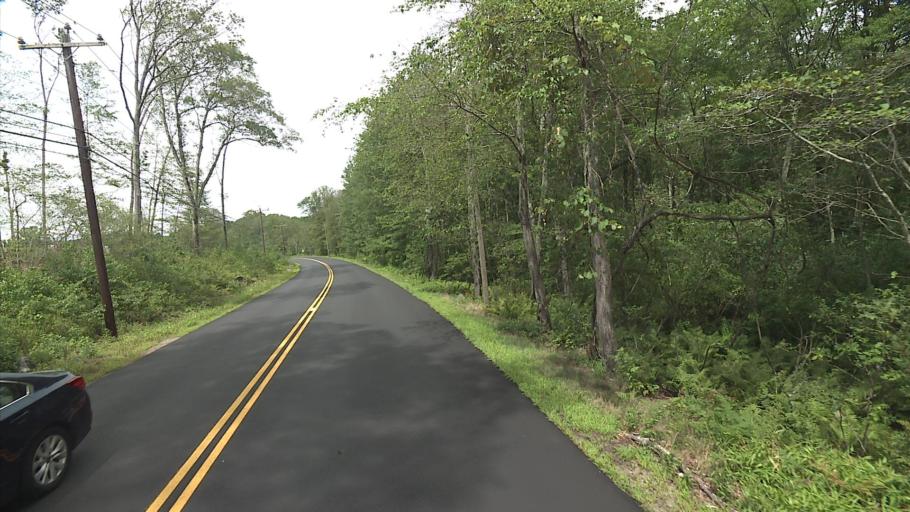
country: US
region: Connecticut
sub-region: Windham County
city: South Woodstock
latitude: 41.9430
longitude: -72.0041
